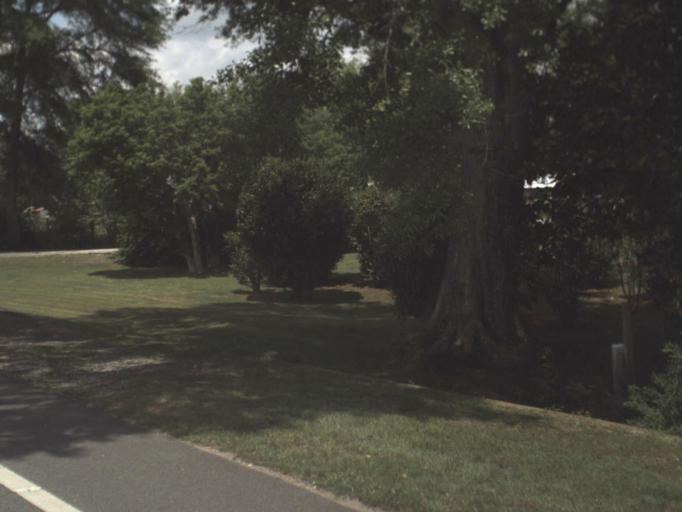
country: US
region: Alabama
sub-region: Escambia County
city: Atmore
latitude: 30.9814
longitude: -87.4916
